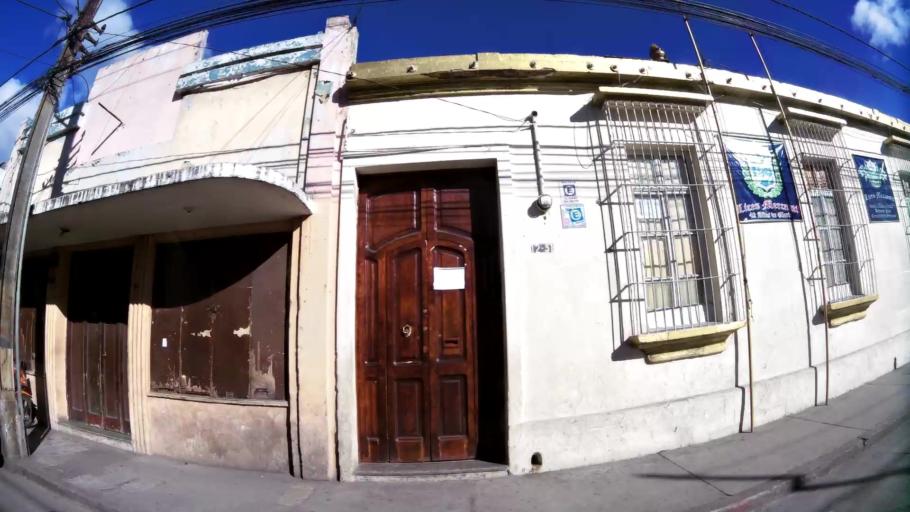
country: GT
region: Guatemala
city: Guatemala City
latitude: 14.6358
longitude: -90.5076
